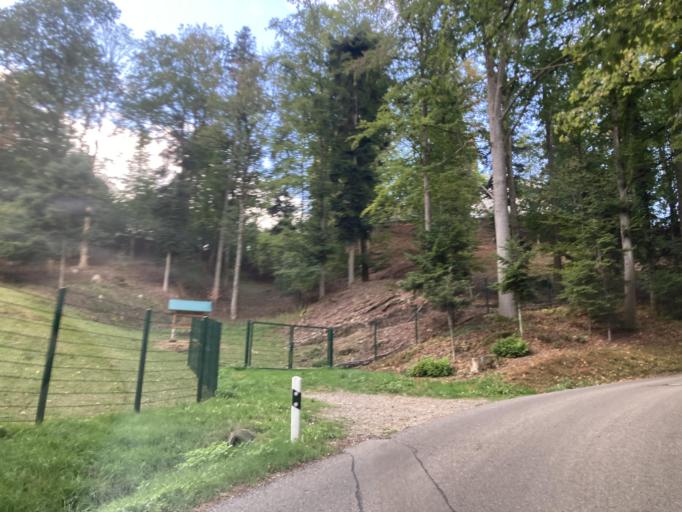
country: DE
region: Baden-Wuerttemberg
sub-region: Karlsruhe Region
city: Buhlertal
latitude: 48.6732
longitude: 8.1592
